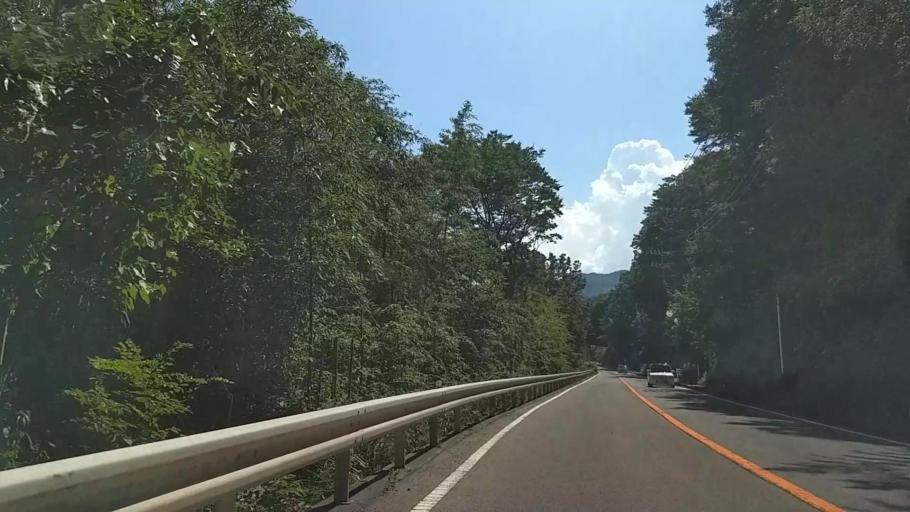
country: JP
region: Yamanashi
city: Ryuo
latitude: 35.4797
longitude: 138.4466
